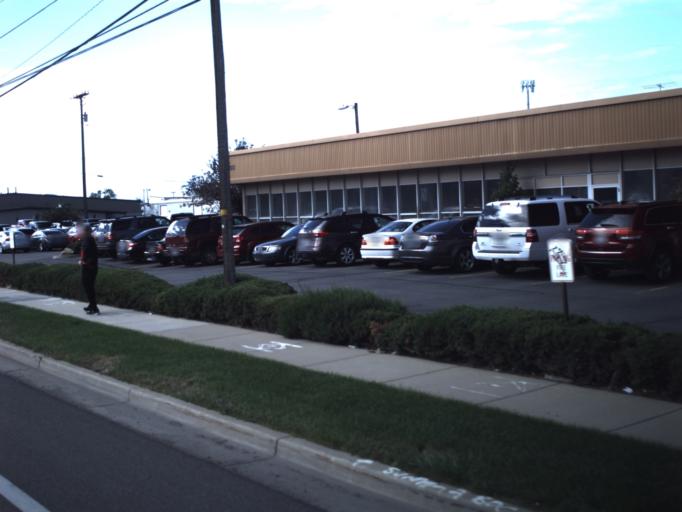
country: US
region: Utah
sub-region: Salt Lake County
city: South Salt Lake
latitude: 40.7362
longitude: -111.9392
